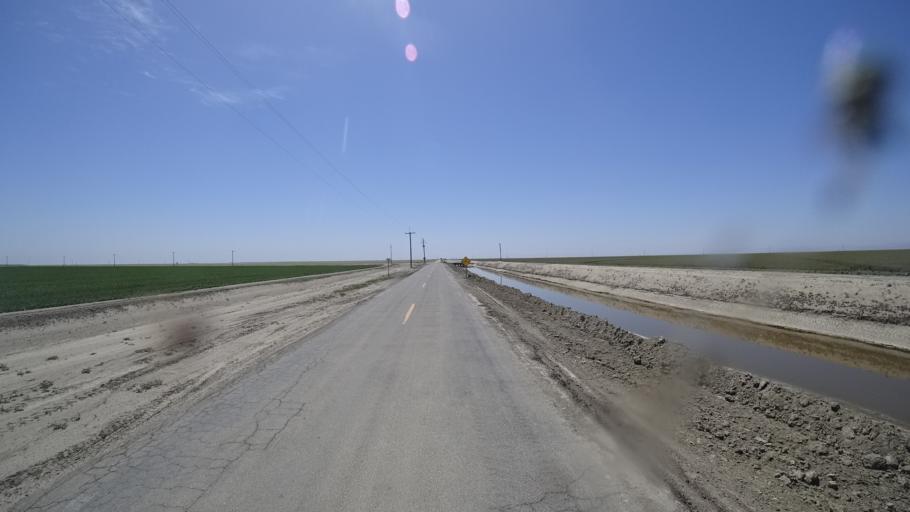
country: US
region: California
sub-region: Kings County
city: Corcoran
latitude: 36.1188
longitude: -119.6801
